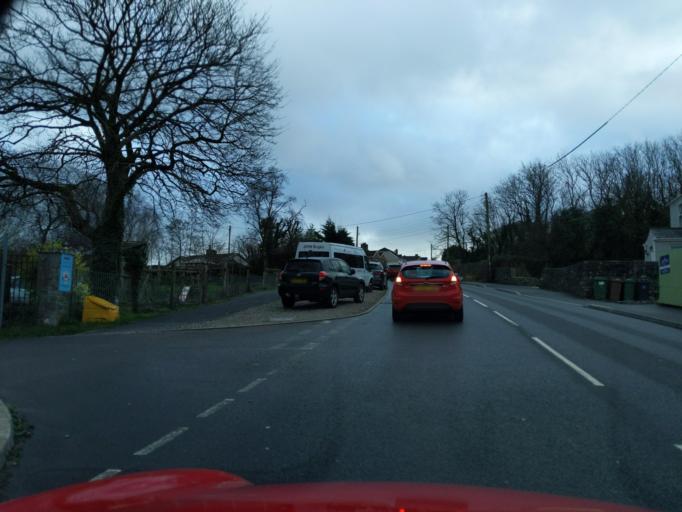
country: GB
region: England
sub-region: Plymouth
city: Plymstock
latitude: 50.3642
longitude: -4.0655
